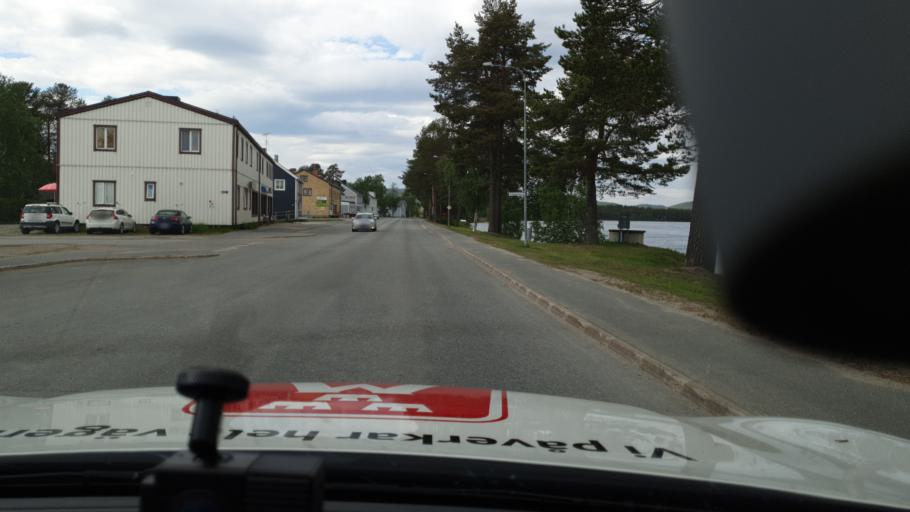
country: SE
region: Vaesterbotten
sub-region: Sorsele Kommun
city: Sorsele
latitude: 65.5371
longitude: 17.5301
